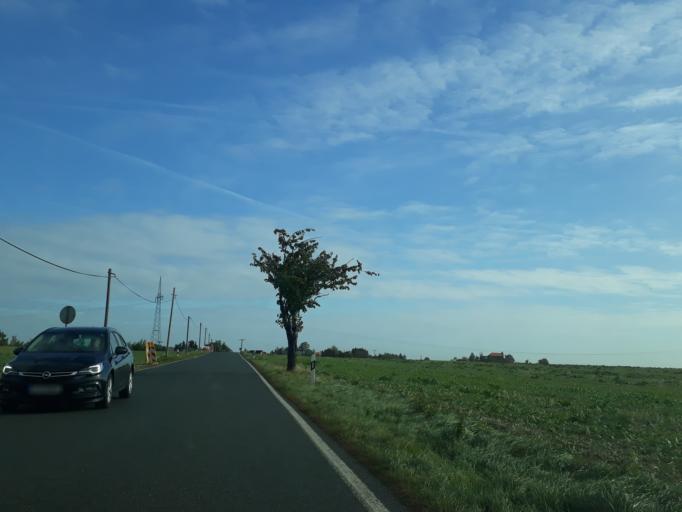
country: DE
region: Saxony
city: Wilsdruff
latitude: 51.0653
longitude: 13.5637
